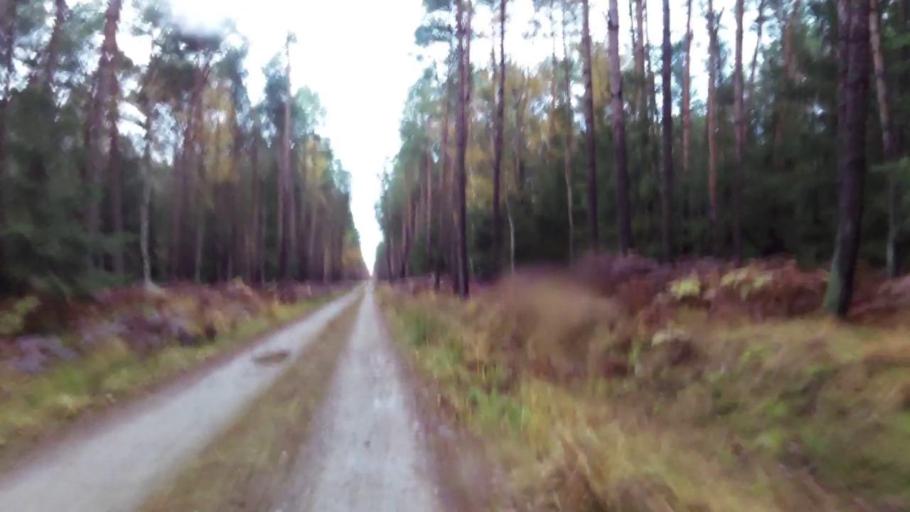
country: PL
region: West Pomeranian Voivodeship
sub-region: Powiat goleniowski
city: Stepnica
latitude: 53.6413
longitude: 14.7061
